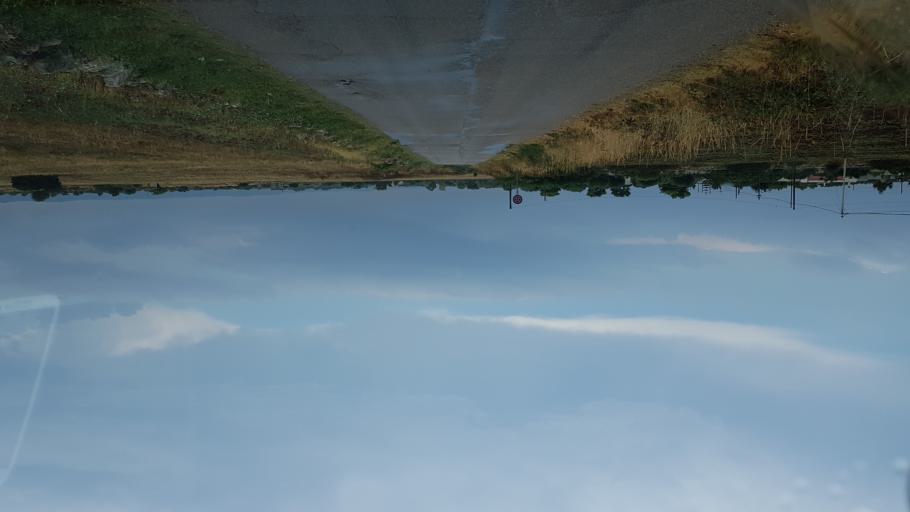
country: IT
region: Apulia
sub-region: Provincia di Bari
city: Monopoli
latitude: 40.9321
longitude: 17.3238
